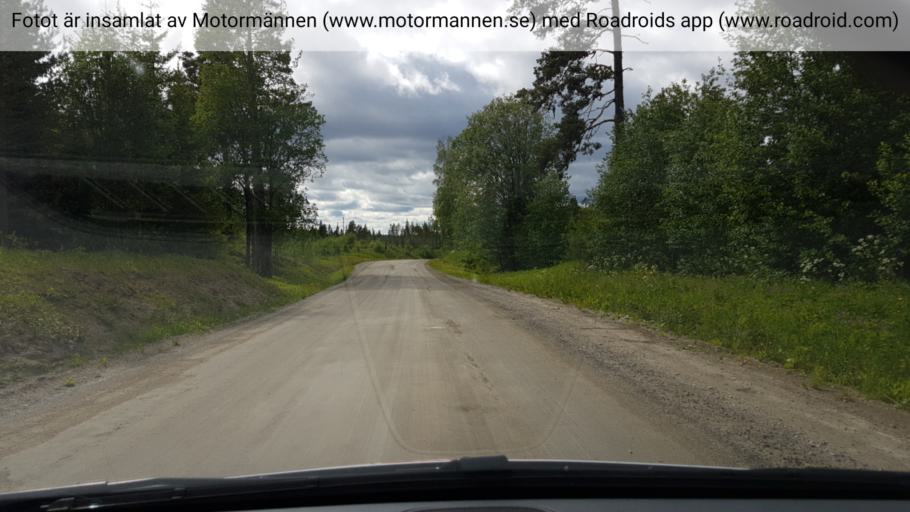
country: SE
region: Jaemtland
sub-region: Braecke Kommun
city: Braecke
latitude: 62.7397
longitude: 15.4449
